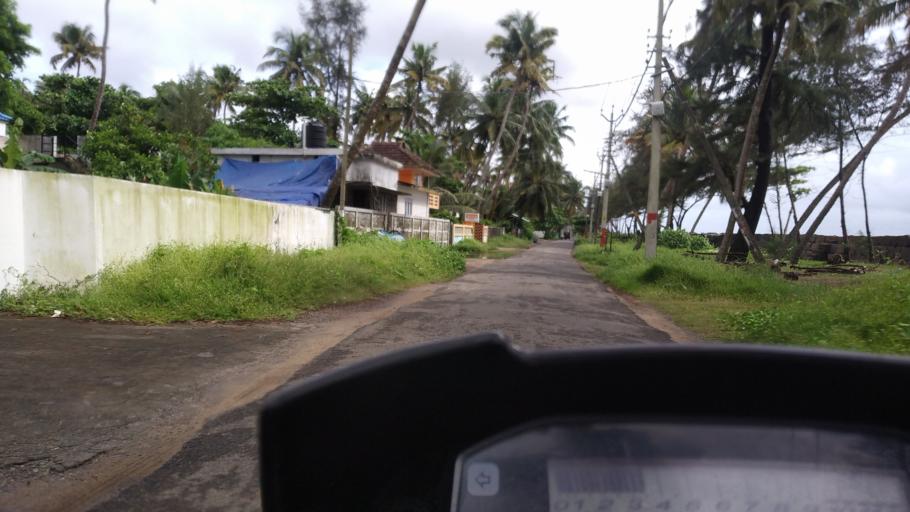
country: IN
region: Kerala
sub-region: Thrissur District
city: Kodungallur
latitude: 10.1582
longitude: 76.1727
